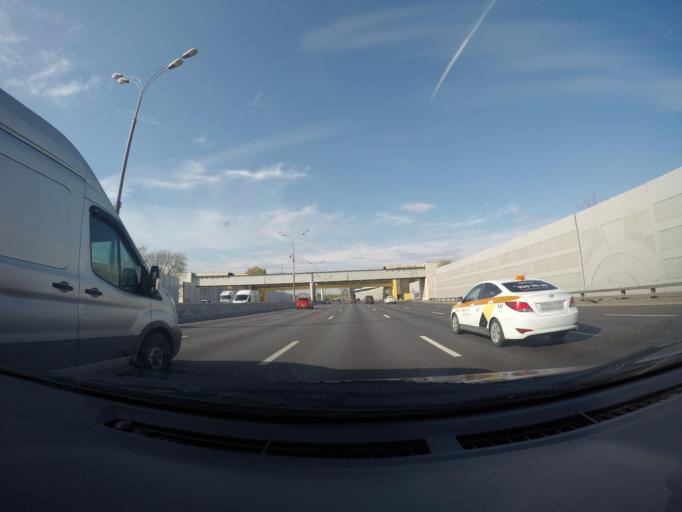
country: RU
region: Moscow
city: Yaroslavskiy
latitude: 55.8926
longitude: 37.7047
